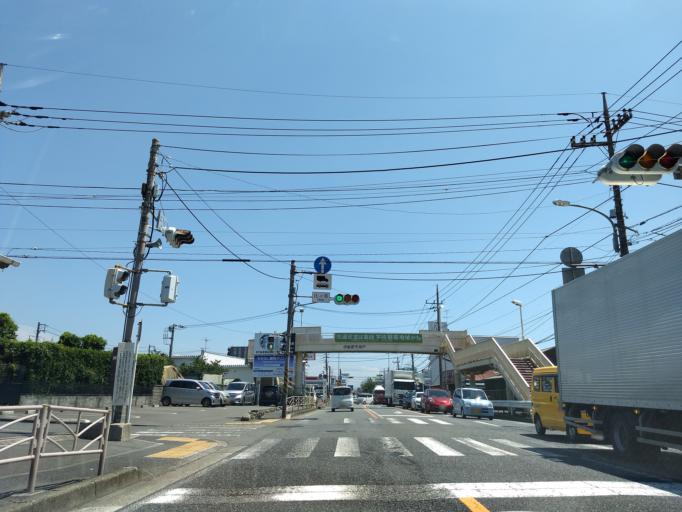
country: JP
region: Kanagawa
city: Isehara
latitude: 35.3945
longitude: 139.2880
